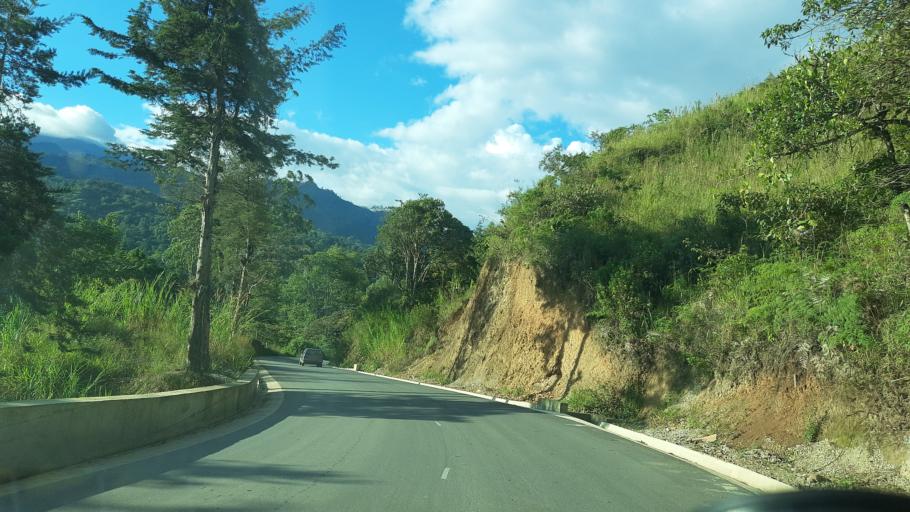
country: CO
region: Boyaca
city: Garagoa
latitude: 5.0806
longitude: -73.3810
